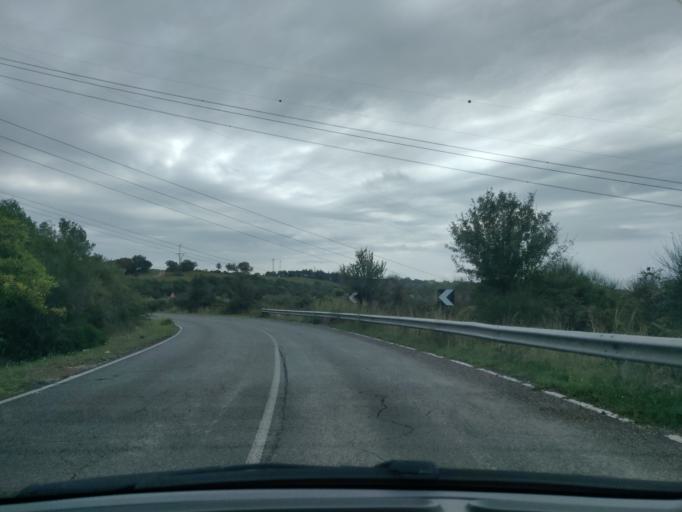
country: IT
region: Latium
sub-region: Citta metropolitana di Roma Capitale
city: Allumiere
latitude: 42.1232
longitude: 11.8630
